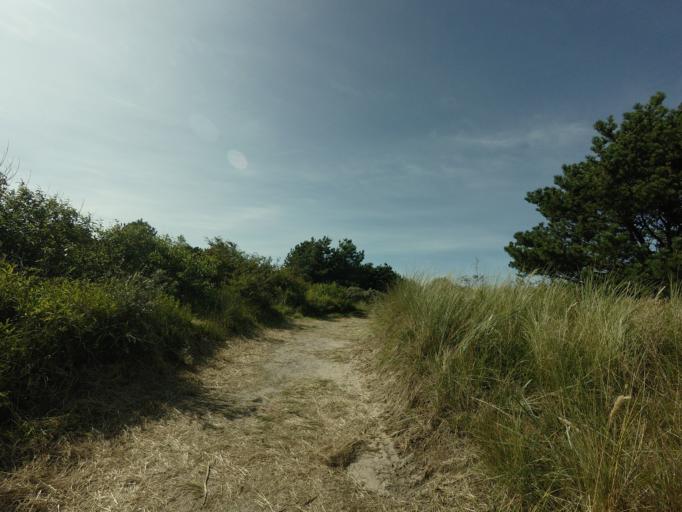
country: NL
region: Friesland
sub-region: Gemeente Ameland
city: Nes
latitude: 53.4553
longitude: 5.7685
